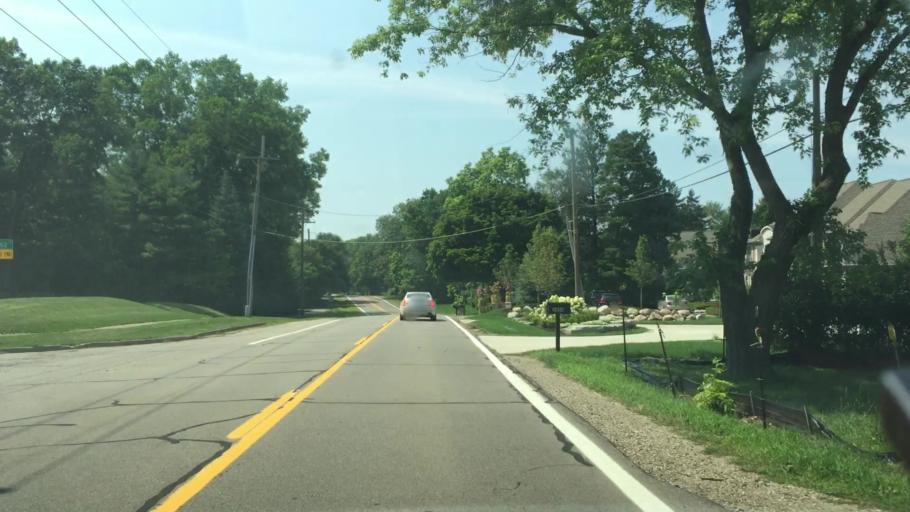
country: US
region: Michigan
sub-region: Oakland County
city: Franklin
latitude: 42.5540
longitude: -83.3308
